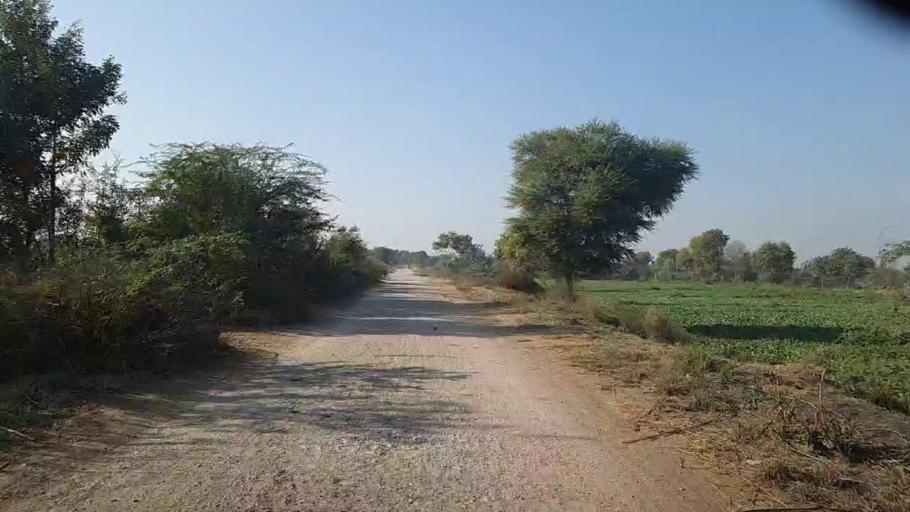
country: PK
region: Sindh
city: Darya Khan Marri
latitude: 26.6772
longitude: 68.3743
